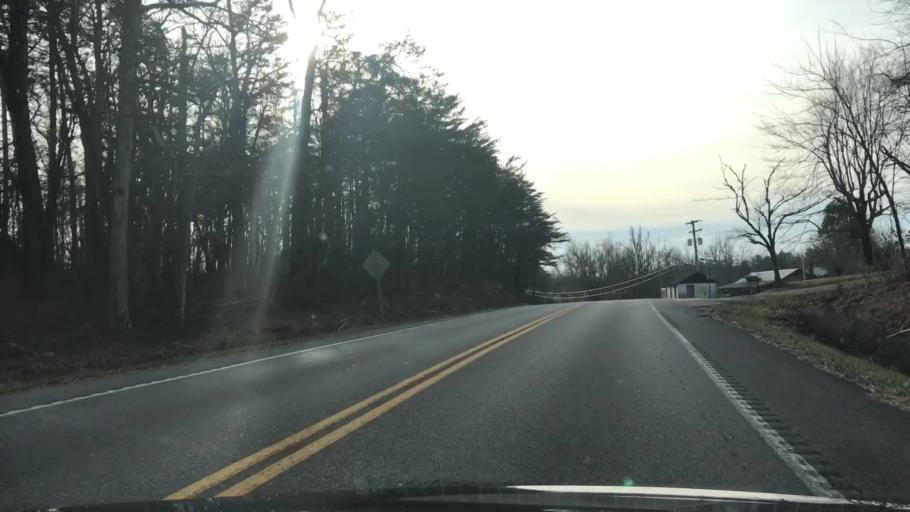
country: US
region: Tennessee
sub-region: Putnam County
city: Monterey
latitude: 36.1376
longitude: -85.2498
